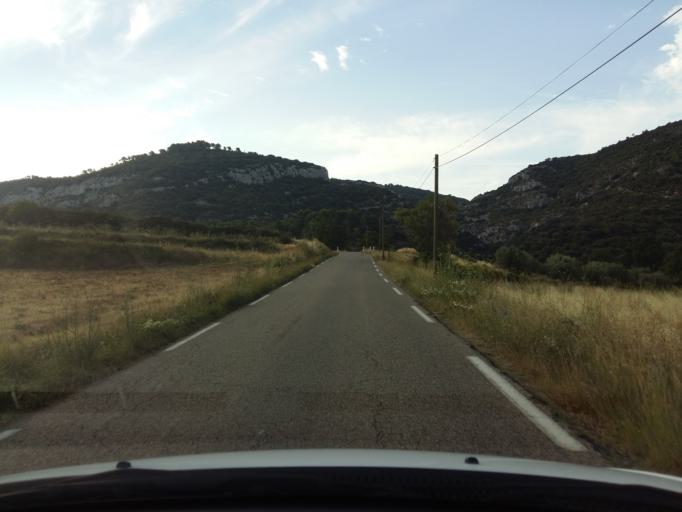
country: FR
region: Provence-Alpes-Cote d'Azur
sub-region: Departement du Vaucluse
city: Venasque
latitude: 43.9855
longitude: 5.1743
